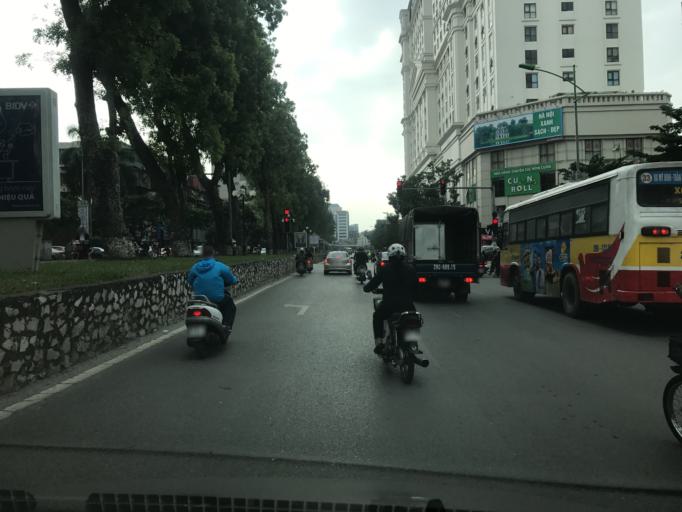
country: VN
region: Ha Noi
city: Dong Da
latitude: 21.0267
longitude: 105.8236
